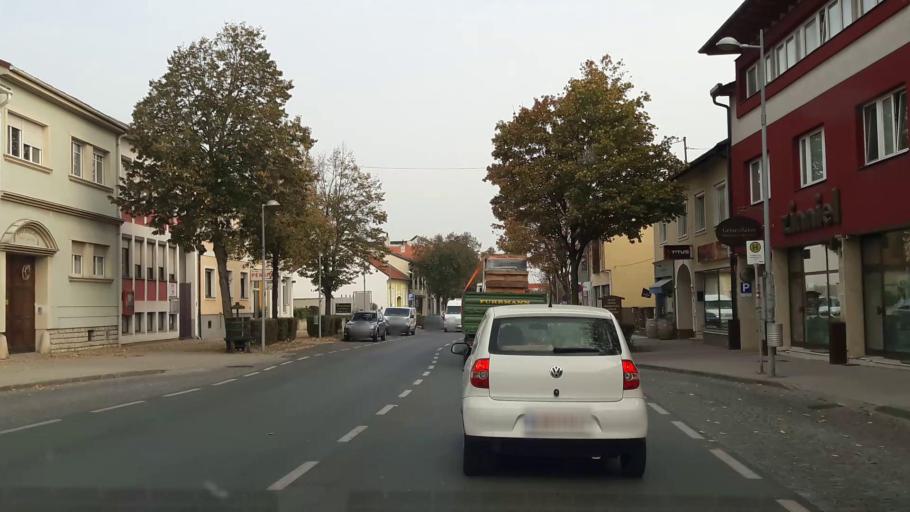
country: AT
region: Burgenland
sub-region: Politischer Bezirk Neusiedl am See
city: Neusiedl am See
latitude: 47.9514
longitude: 16.8371
